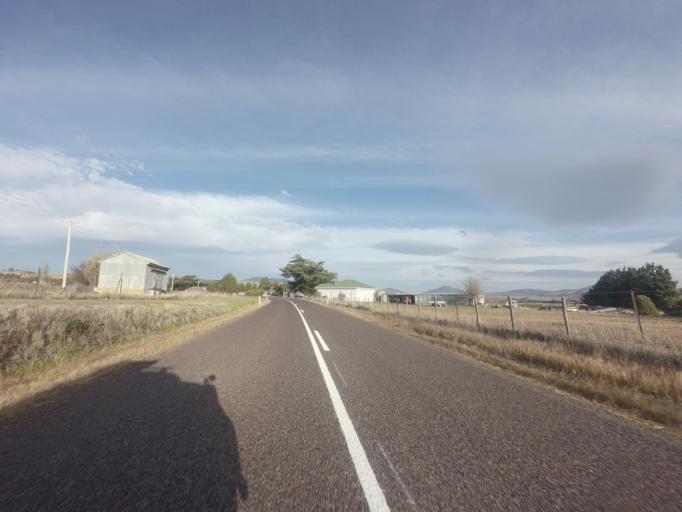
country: AU
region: Tasmania
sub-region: Brighton
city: Bridgewater
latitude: -42.4694
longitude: 147.1771
